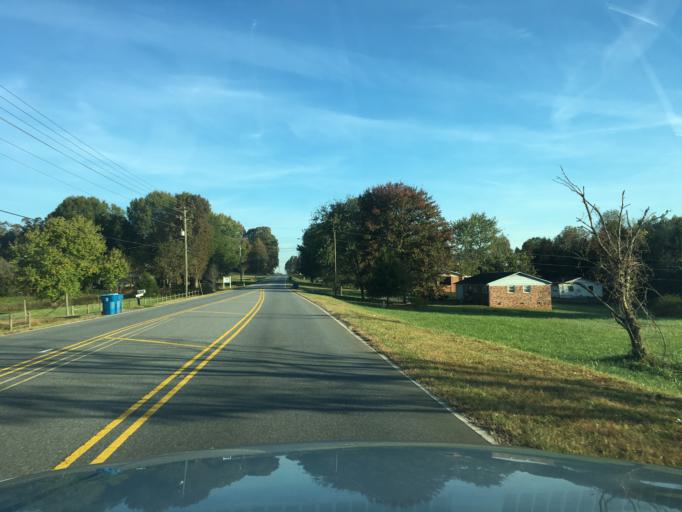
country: US
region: North Carolina
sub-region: Catawba County
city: Maiden
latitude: 35.6005
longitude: -81.2549
